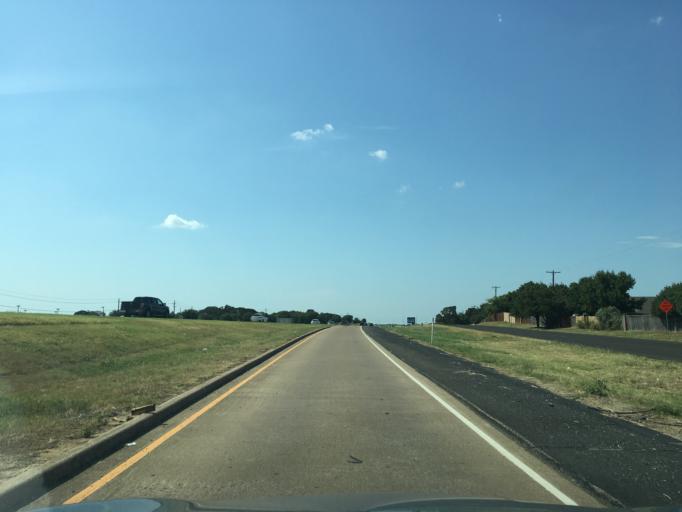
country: US
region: Texas
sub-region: Tarrant County
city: Kennedale
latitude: 32.6359
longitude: -97.1777
